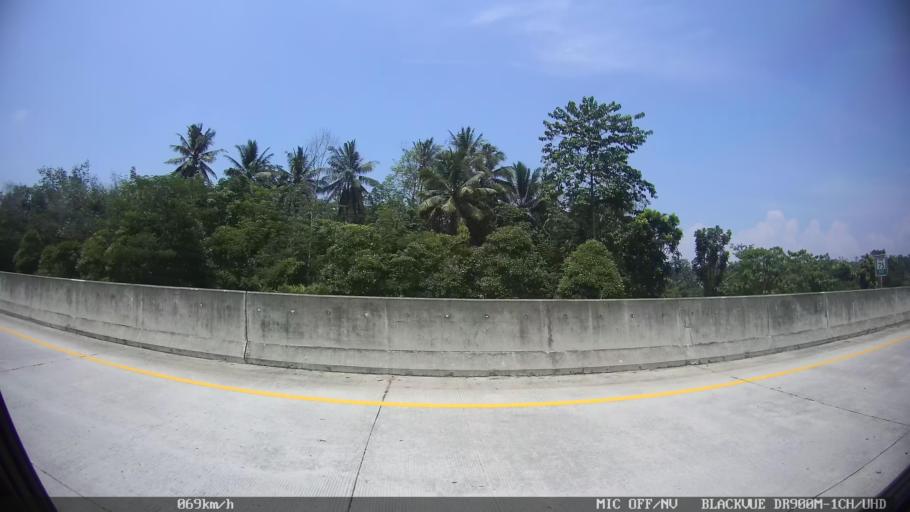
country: ID
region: Lampung
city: Kedaton
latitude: -5.3873
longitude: 105.3397
